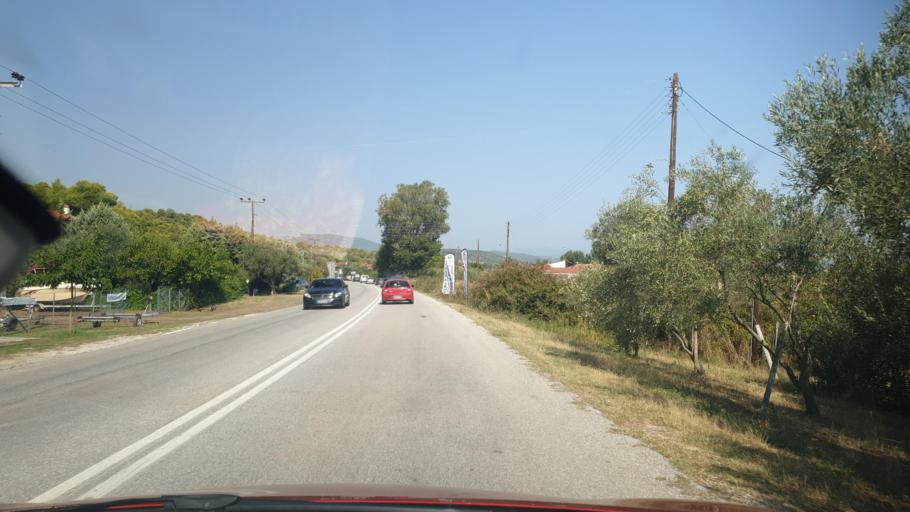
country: GR
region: Central Macedonia
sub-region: Nomos Chalkidikis
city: Agios Nikolaos
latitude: 40.2264
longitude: 23.7426
